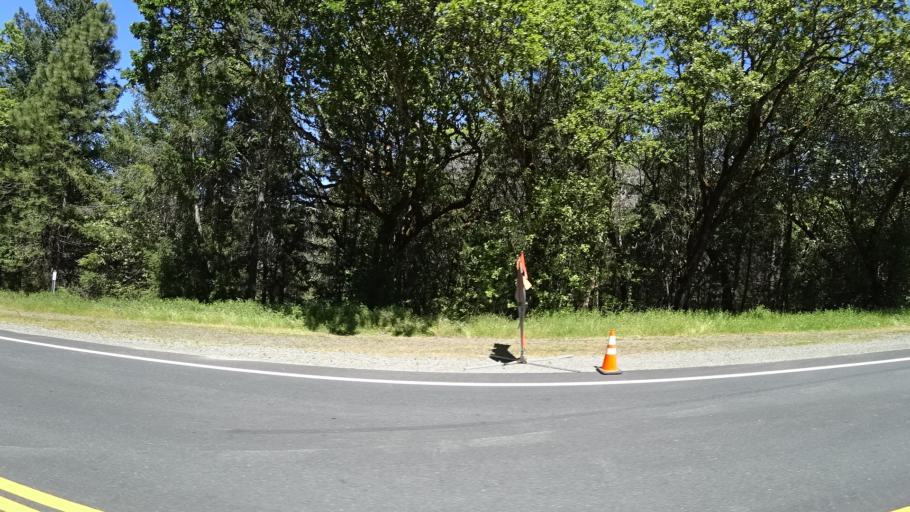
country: US
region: California
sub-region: Humboldt County
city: Willow Creek
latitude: 40.8101
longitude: -123.4761
